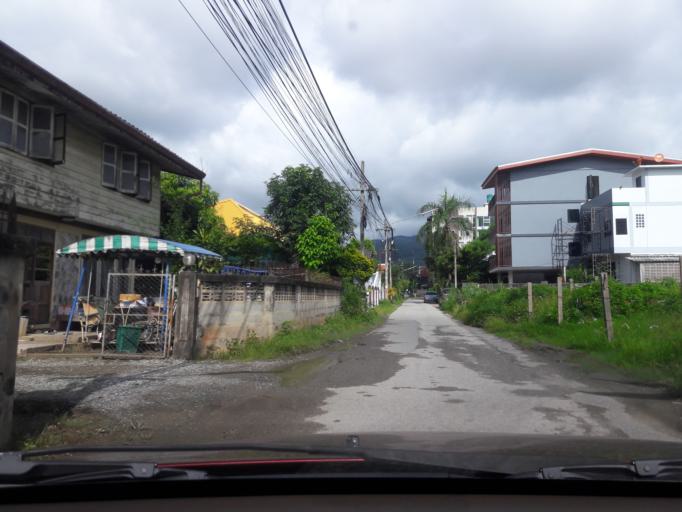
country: TH
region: Chiang Mai
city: Chiang Mai
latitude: 18.7852
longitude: 98.9696
